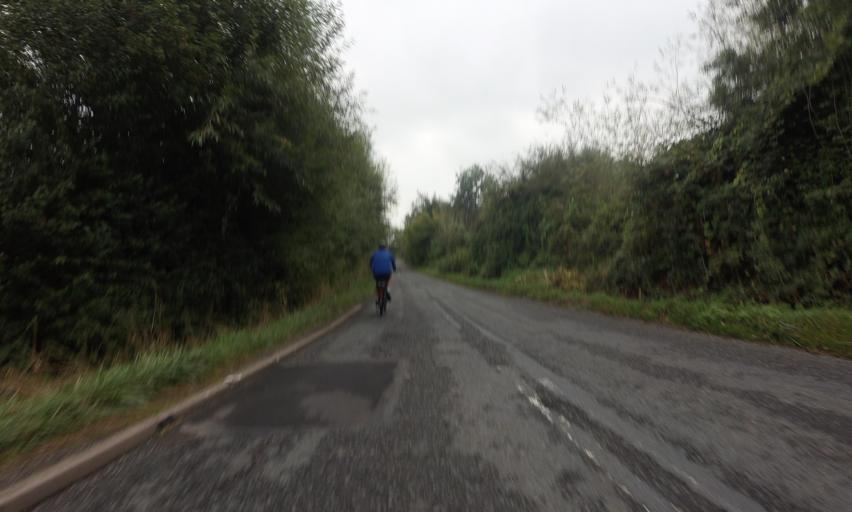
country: GB
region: England
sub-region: Gloucestershire
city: Winchcombe
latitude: 51.9650
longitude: -1.9711
